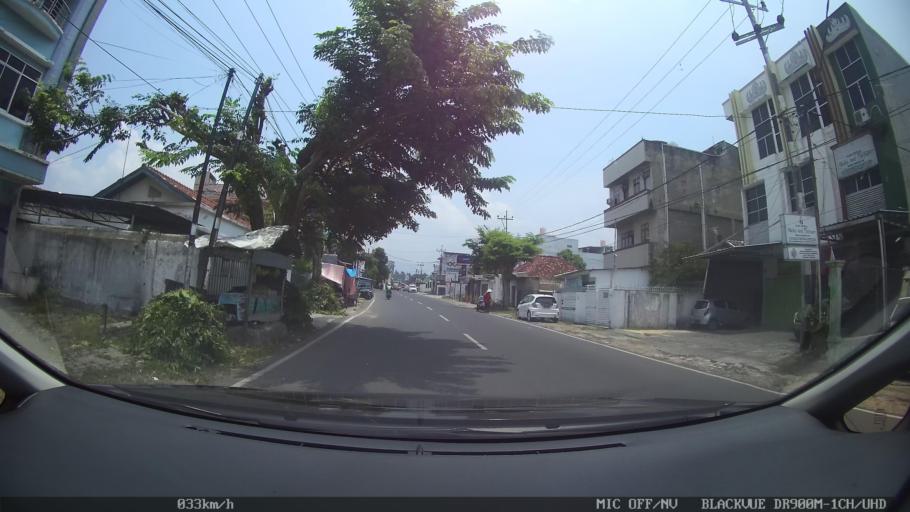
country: ID
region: Lampung
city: Bandarlampung
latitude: -5.4396
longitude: 105.2690
